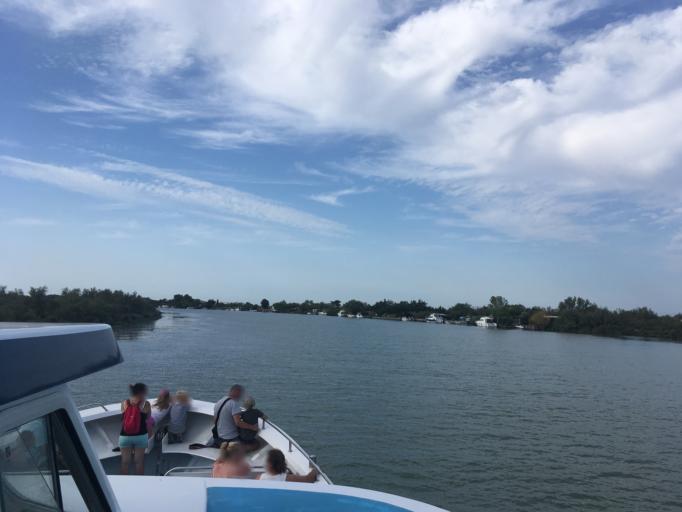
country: FR
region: Provence-Alpes-Cote d'Azur
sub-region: Departement des Bouches-du-Rhone
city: Saintes-Maries-de-la-Mer
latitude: 43.4657
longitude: 4.3929
